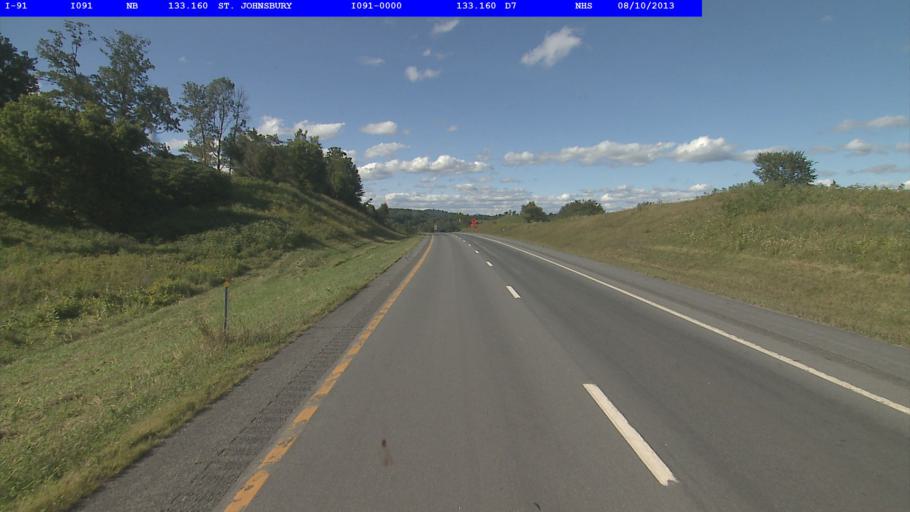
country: US
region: Vermont
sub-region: Caledonia County
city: St Johnsbury
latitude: 44.4625
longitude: -72.0233
